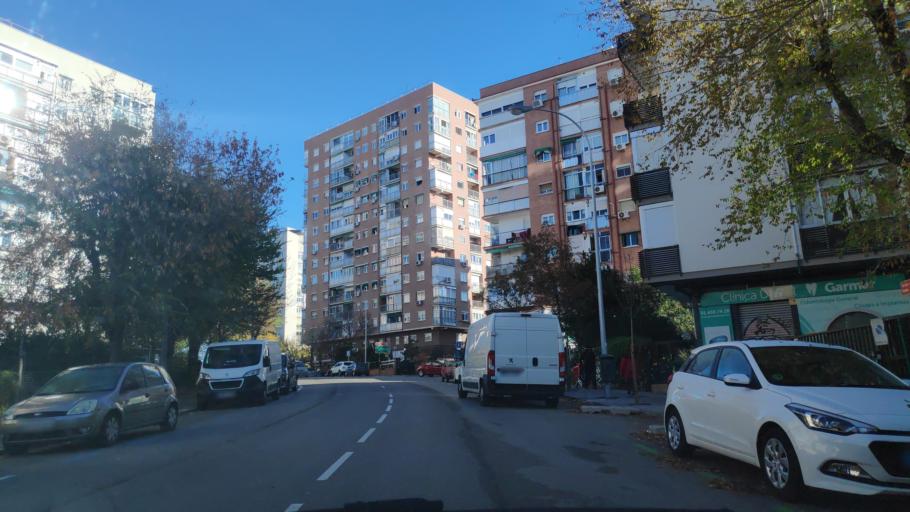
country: ES
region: Madrid
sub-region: Provincia de Madrid
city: Tetuan de las Victorias
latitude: 40.4566
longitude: -3.7136
